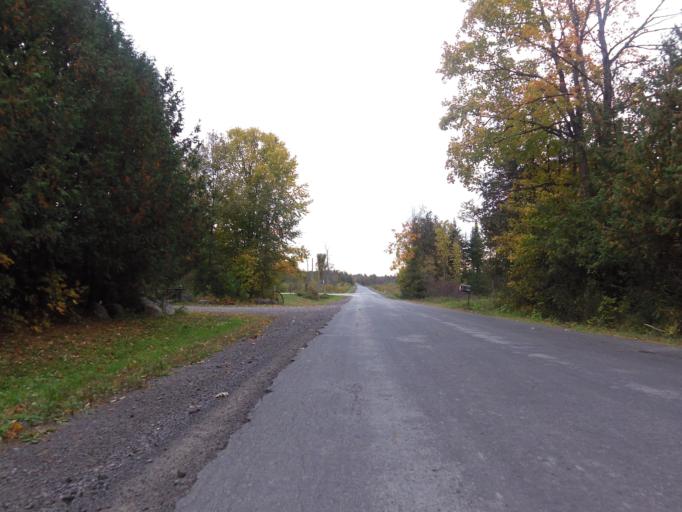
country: CA
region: Ontario
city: Arnprior
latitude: 45.4581
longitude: -76.1409
